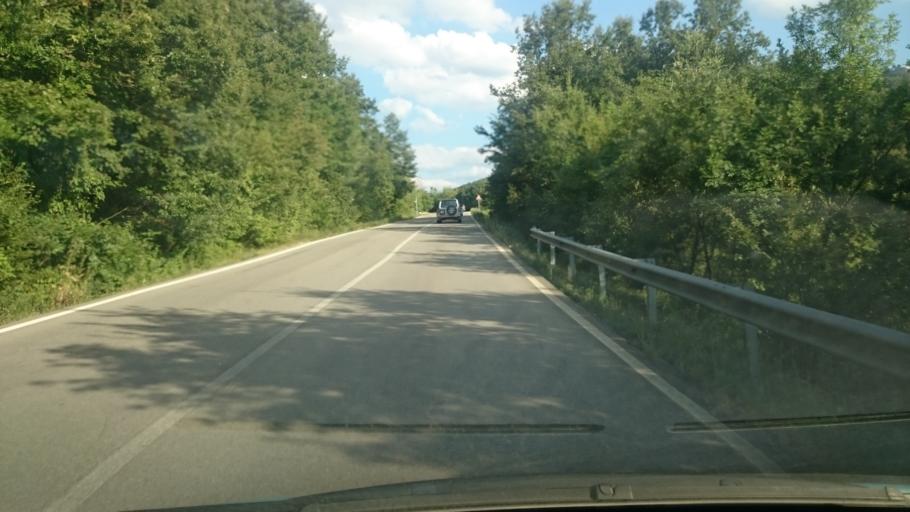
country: IT
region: Emilia-Romagna
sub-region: Provincia di Reggio Emilia
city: Toano
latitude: 44.4121
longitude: 10.5961
